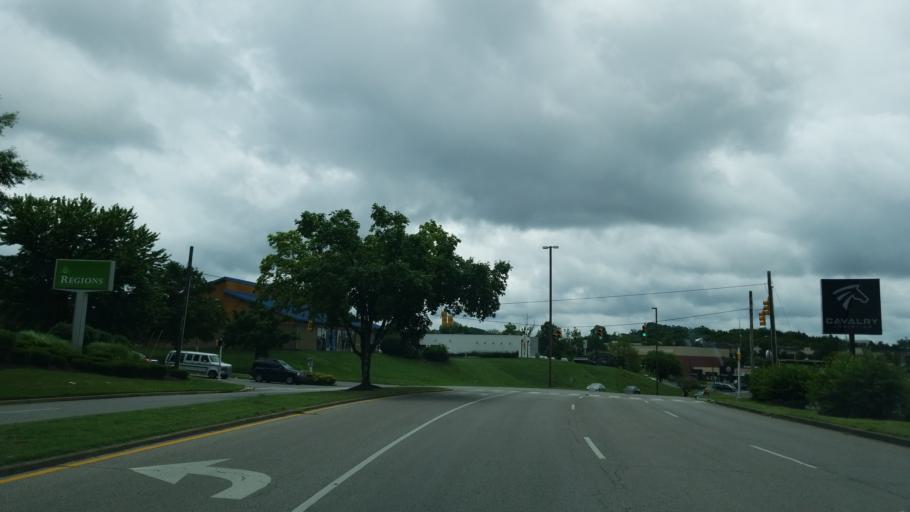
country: US
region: Tennessee
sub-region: Rutherford County
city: La Vergne
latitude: 36.0485
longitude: -86.6582
